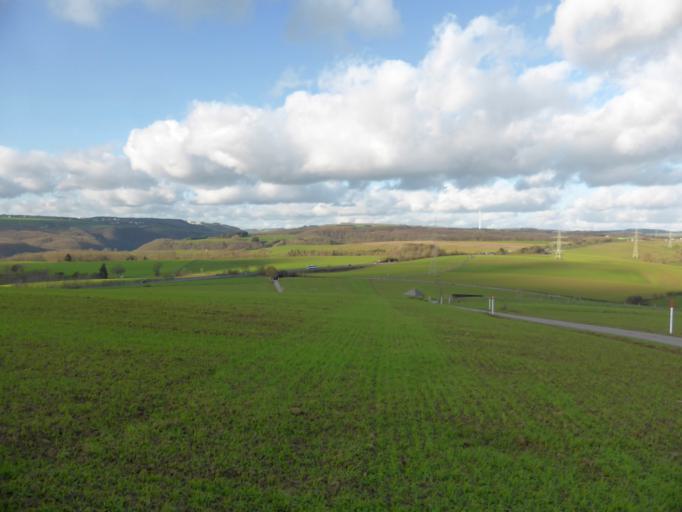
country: LU
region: Diekirch
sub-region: Canton de Diekirch
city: Erpeldange
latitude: 49.8627
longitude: 6.1302
